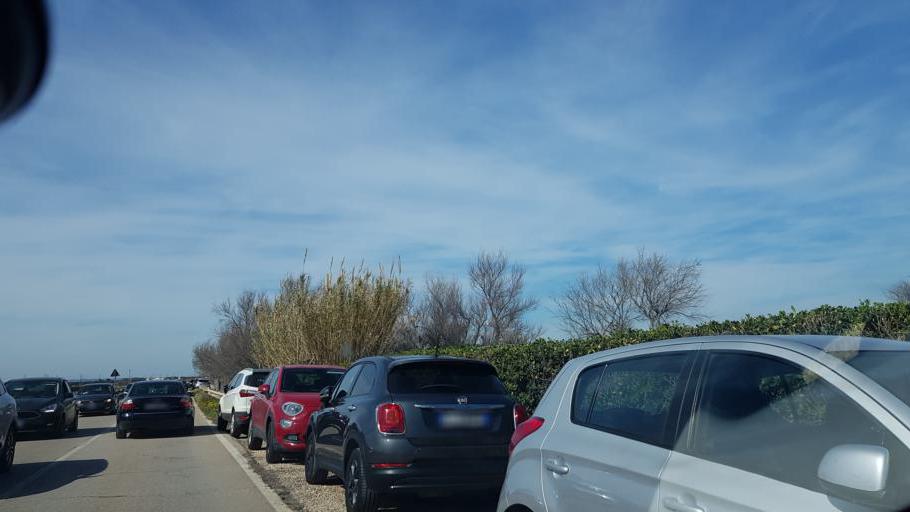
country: IT
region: Apulia
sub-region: Provincia di Brindisi
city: Pezze di Greco
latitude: 40.8570
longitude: 17.4366
